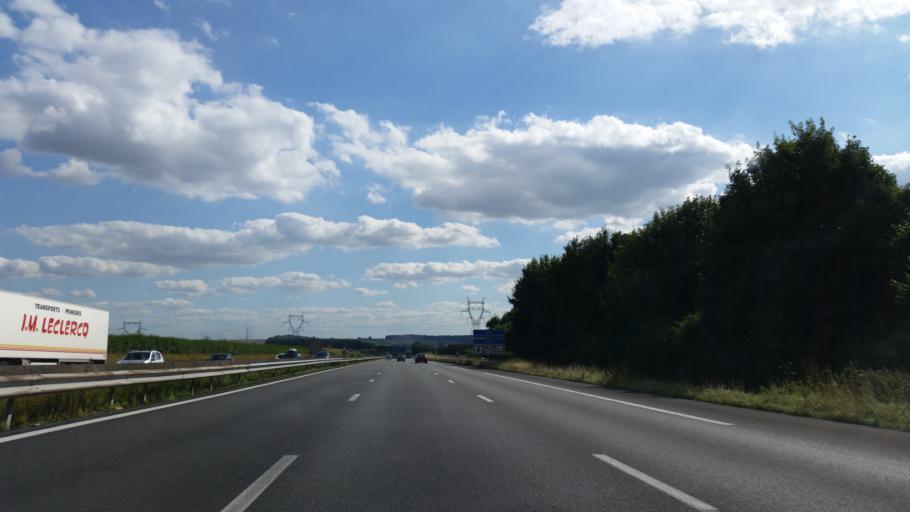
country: FR
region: Picardie
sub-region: Departement de la Somme
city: Peronne
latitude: 49.9804
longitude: 2.8673
